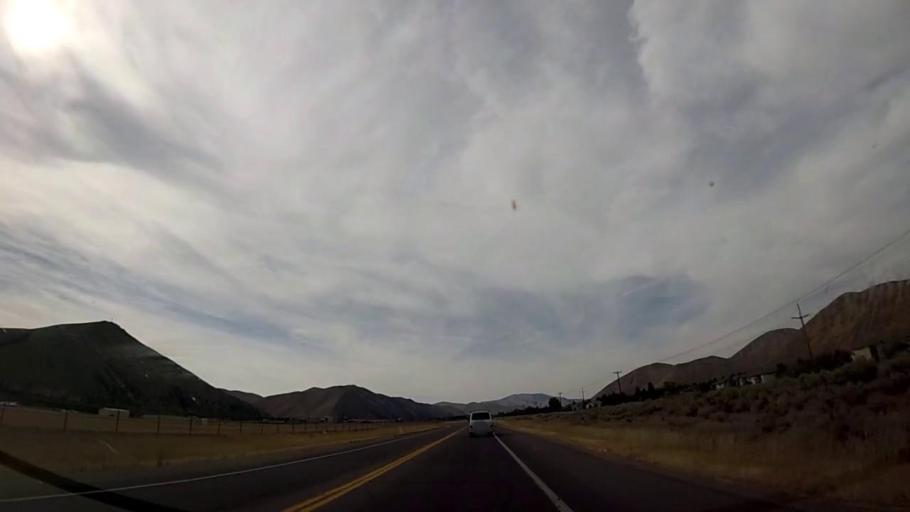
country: US
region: Idaho
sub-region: Blaine County
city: Hailey
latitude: 43.5010
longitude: -114.2911
